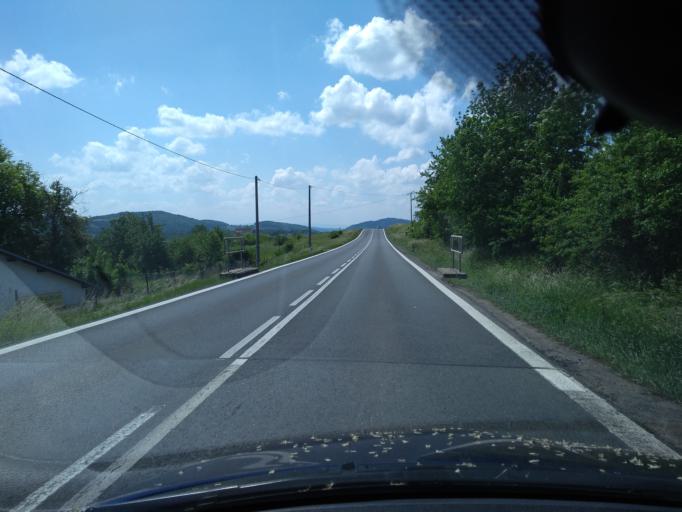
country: CZ
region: Plzensky
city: Prestice
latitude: 49.5660
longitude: 13.3249
